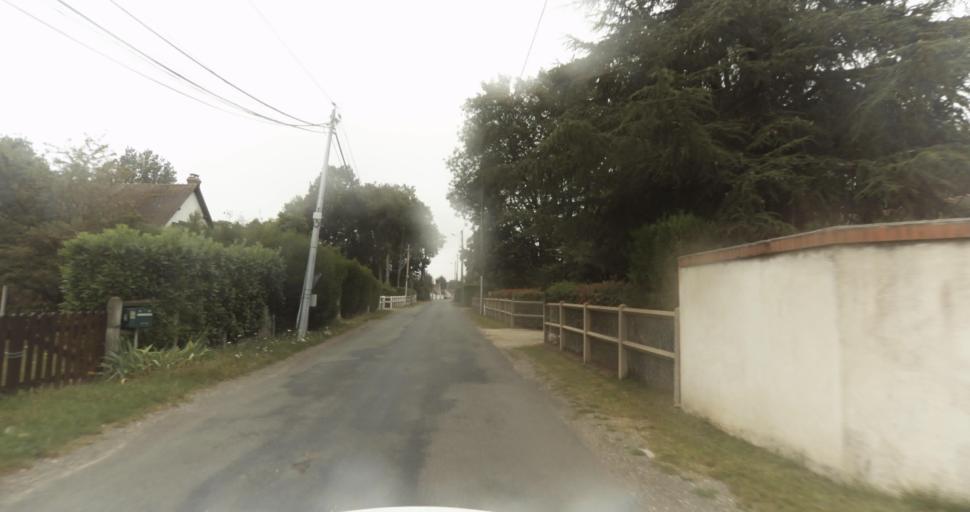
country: FR
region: Haute-Normandie
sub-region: Departement de l'Eure
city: Saint-Germain-sur-Avre
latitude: 48.7729
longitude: 1.2623
